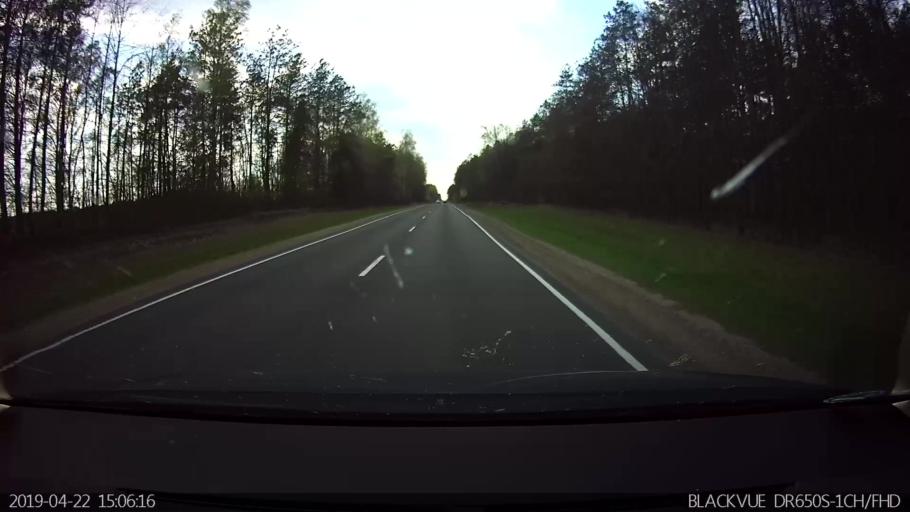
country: BY
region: Brest
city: Kamyanyets
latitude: 52.3320
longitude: 23.8422
